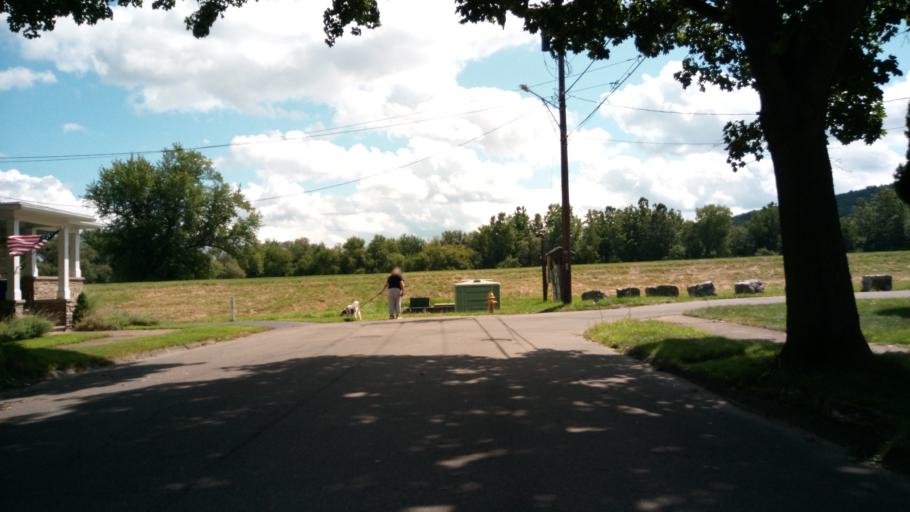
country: US
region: New York
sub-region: Chemung County
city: West Elmira
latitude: 42.0807
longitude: -76.8257
